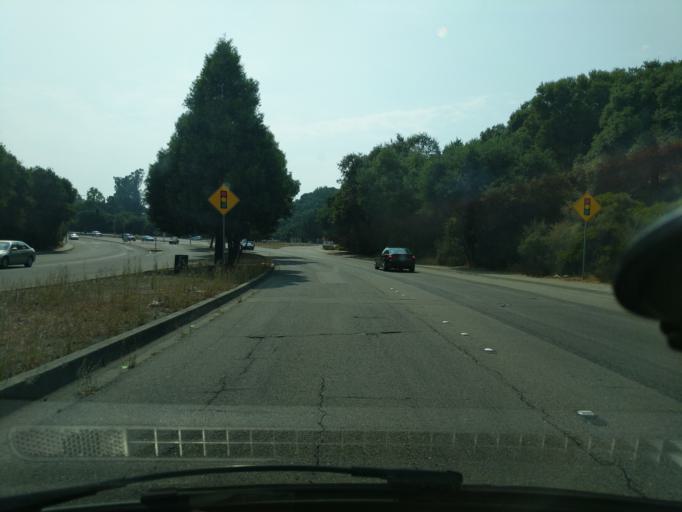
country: US
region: California
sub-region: Alameda County
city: Fairview
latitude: 37.7029
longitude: -122.0521
